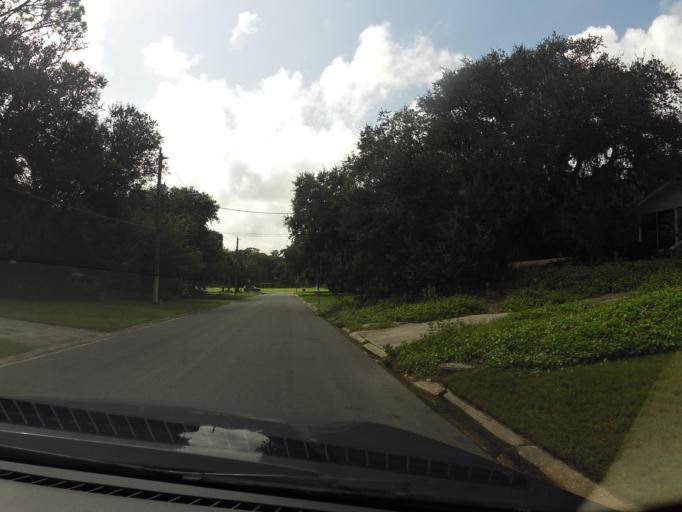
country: US
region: Florida
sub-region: Nassau County
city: Fernandina Beach
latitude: 30.6661
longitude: -81.4344
